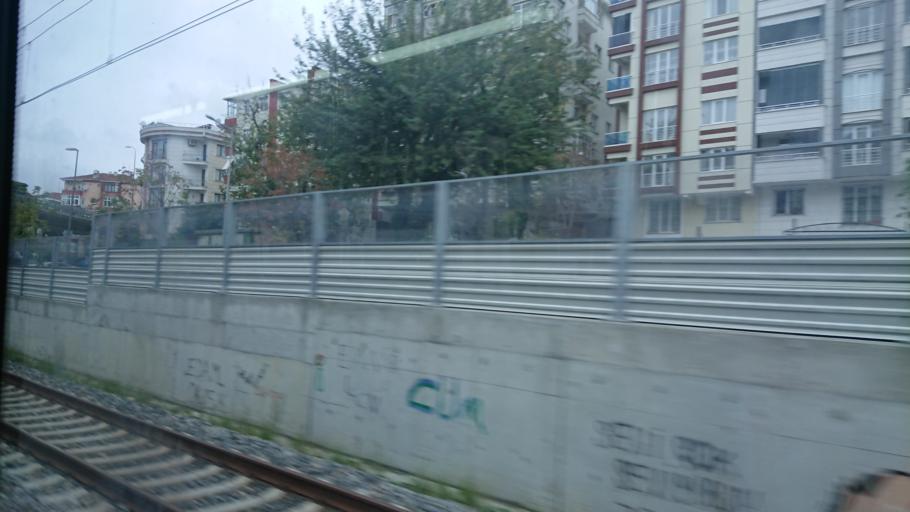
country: TR
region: Istanbul
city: Mahmutbey
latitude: 40.9933
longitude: 28.7698
